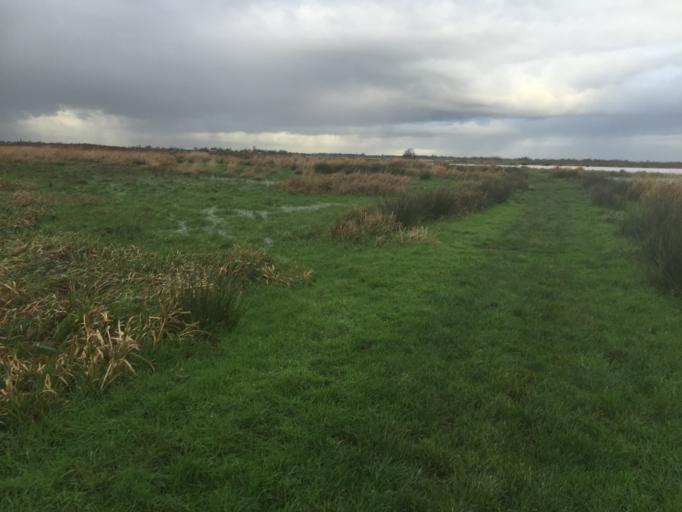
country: NL
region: South Holland
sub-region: Gemeente Nieuwkoop
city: Nieuwkoop
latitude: 52.1571
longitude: 4.7902
